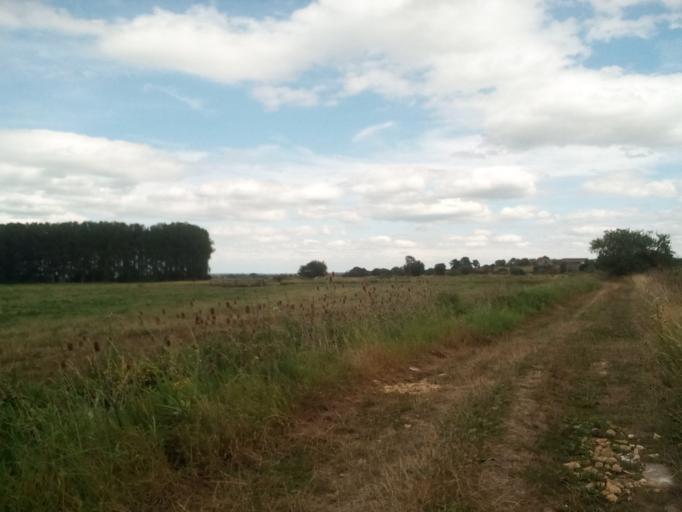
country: FR
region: Lower Normandy
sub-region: Departement du Calvados
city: Troarn
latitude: 49.1719
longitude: -0.1492
